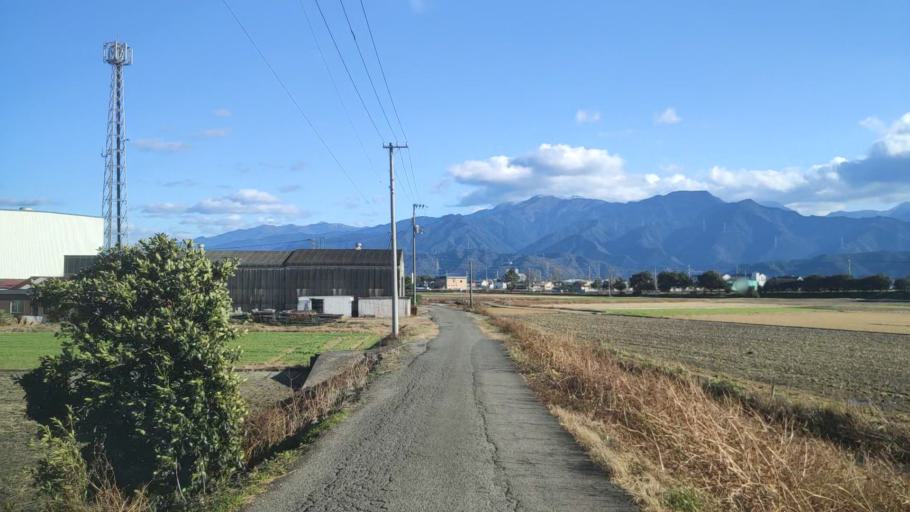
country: JP
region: Ehime
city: Saijo
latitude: 33.9207
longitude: 133.1566
